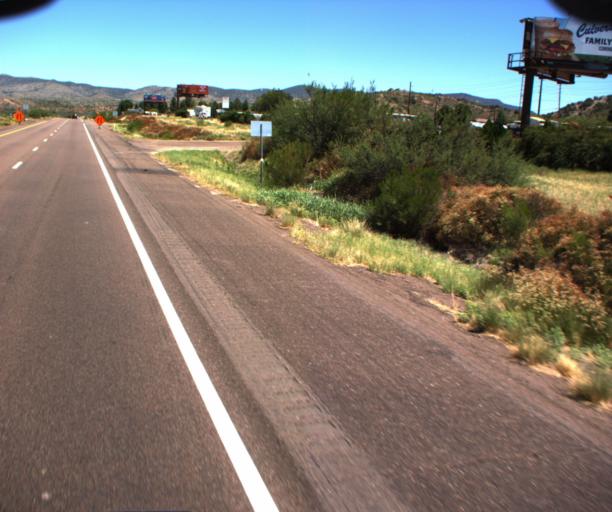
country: US
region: Arizona
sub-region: Gila County
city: Payson
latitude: 34.1018
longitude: -111.3534
